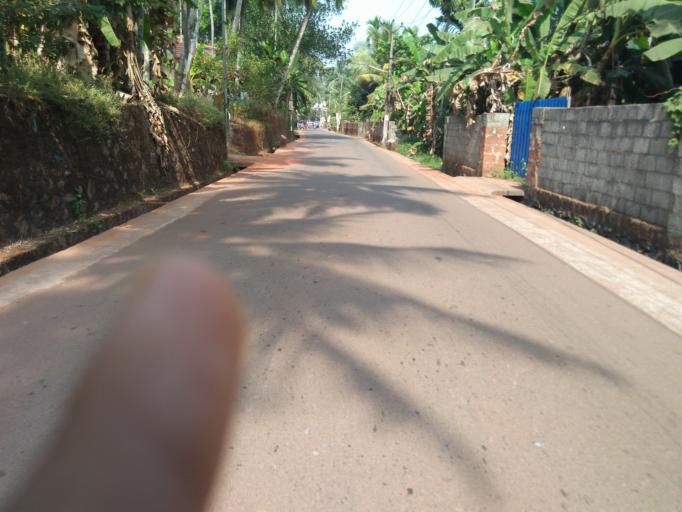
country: IN
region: Kerala
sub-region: Kozhikode
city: Kunnamangalam
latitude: 11.2943
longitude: 75.8365
